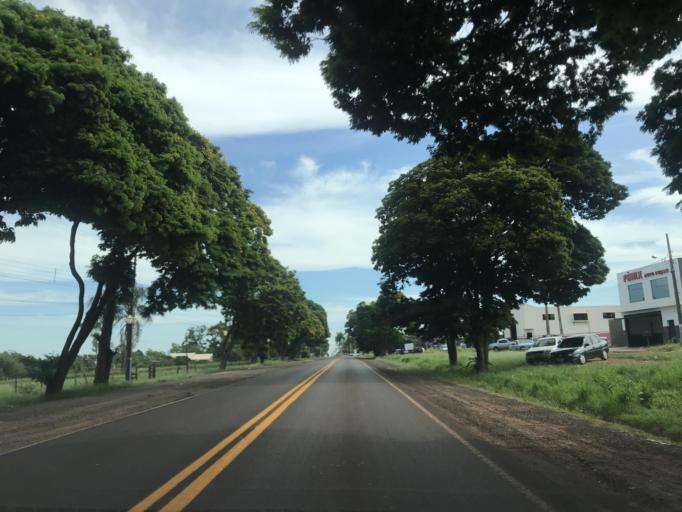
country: BR
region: Parana
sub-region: Terra Rica
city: Terra Rica
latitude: -22.7369
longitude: -52.6246
